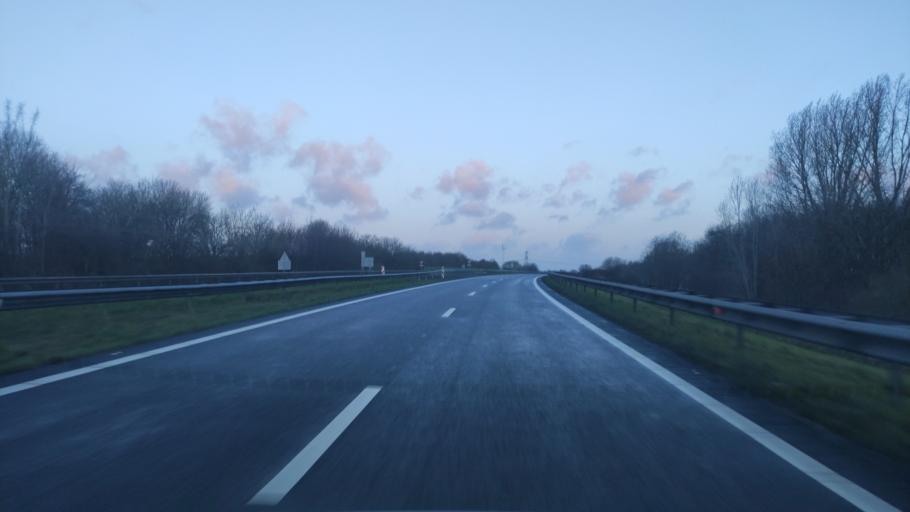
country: NL
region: Gelderland
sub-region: Gemeente Harderwijk
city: Harderwijk
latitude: 52.4087
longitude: 5.5894
